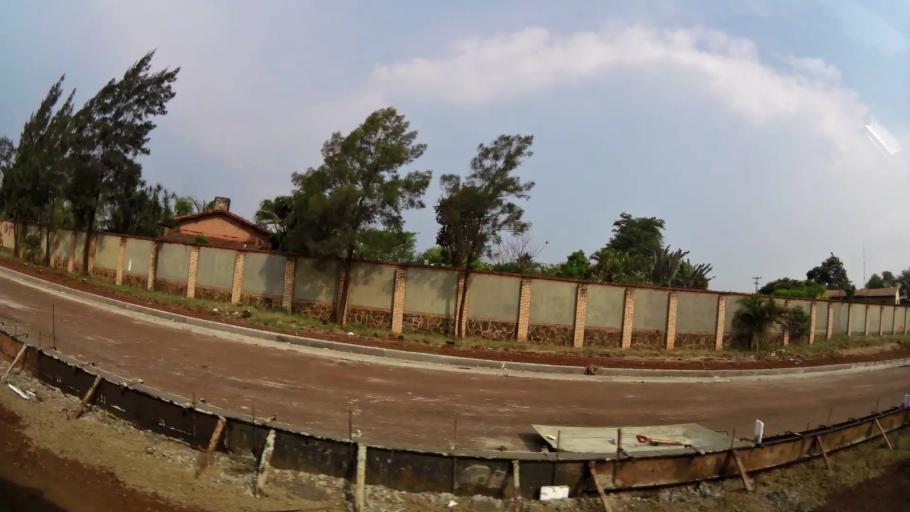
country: PY
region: Alto Parana
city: Ciudad del Este
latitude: -25.4791
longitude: -54.6559
